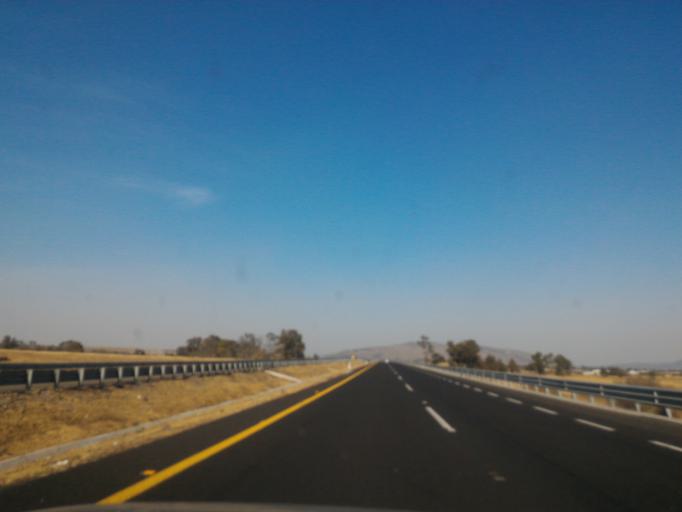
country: MX
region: Mexico
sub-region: Jilotepec
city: Xhixhata
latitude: 19.9654
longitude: -99.5408
